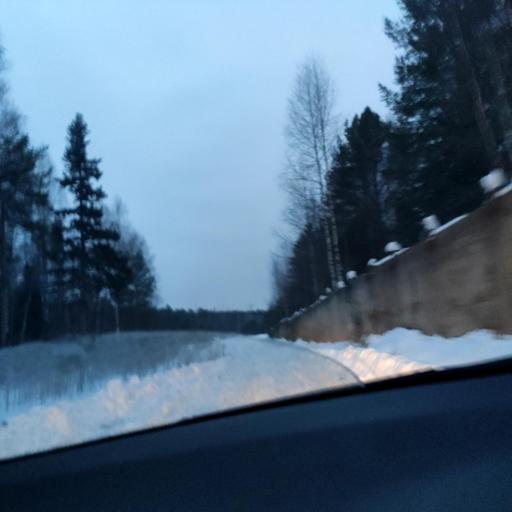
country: RU
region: Perm
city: Overyata
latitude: 58.0419
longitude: 55.8622
